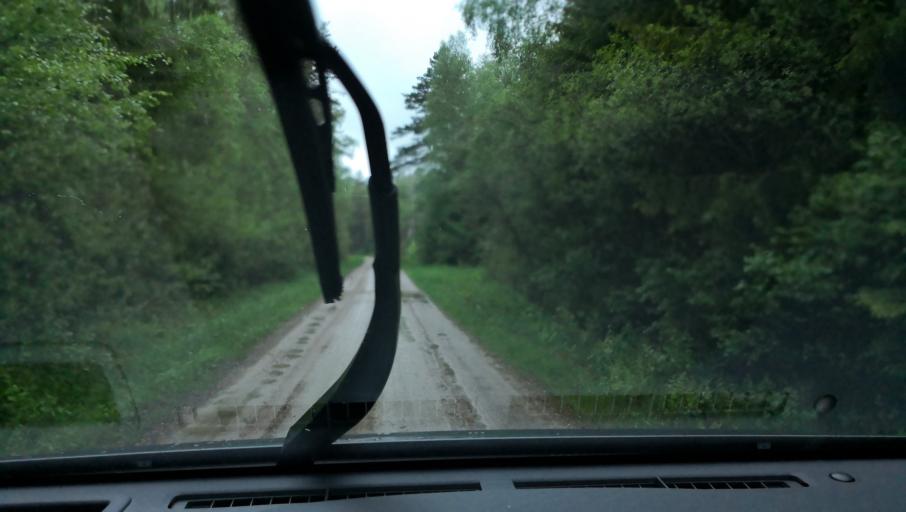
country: SE
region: Uppsala
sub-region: Enkopings Kommun
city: Orsundsbro
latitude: 59.9255
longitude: 17.3373
